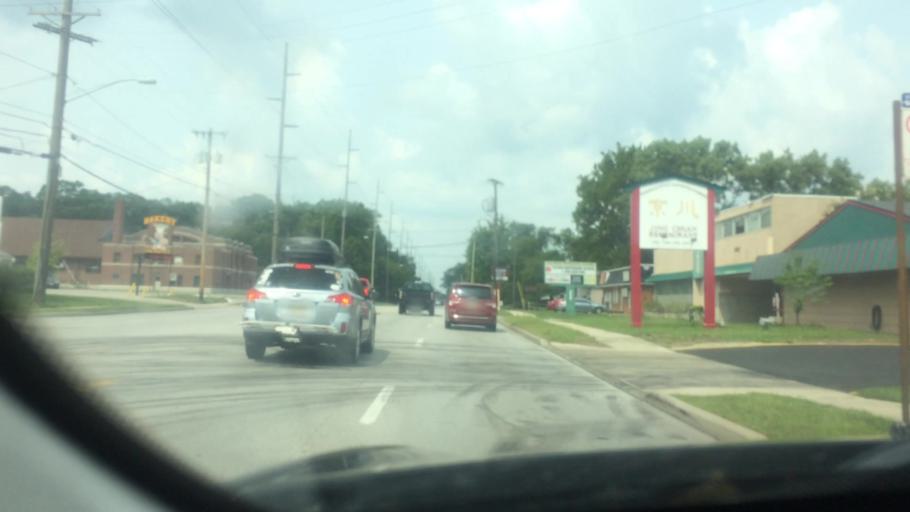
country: US
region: Ohio
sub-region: Lucas County
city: Ottawa Hills
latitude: 41.6977
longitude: -83.6233
